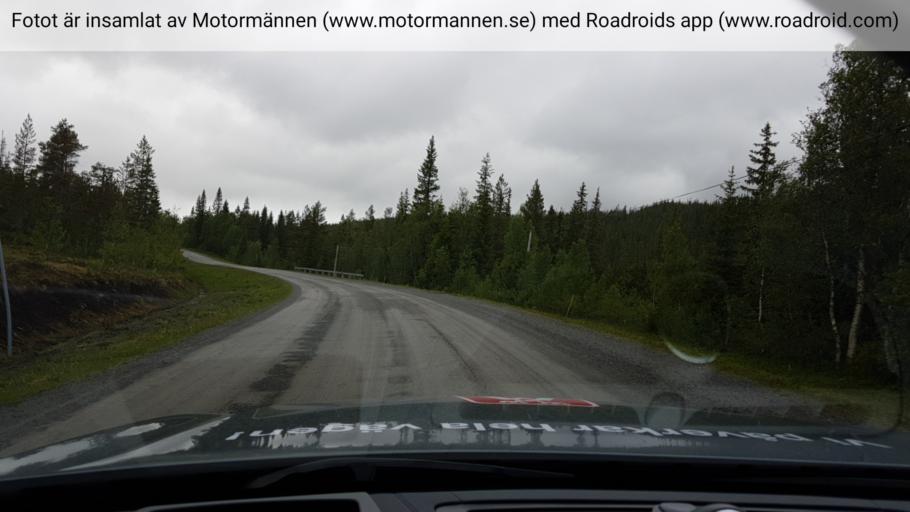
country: NO
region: Nord-Trondelag
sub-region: Snasa
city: Snaase
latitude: 63.7224
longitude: 12.6069
